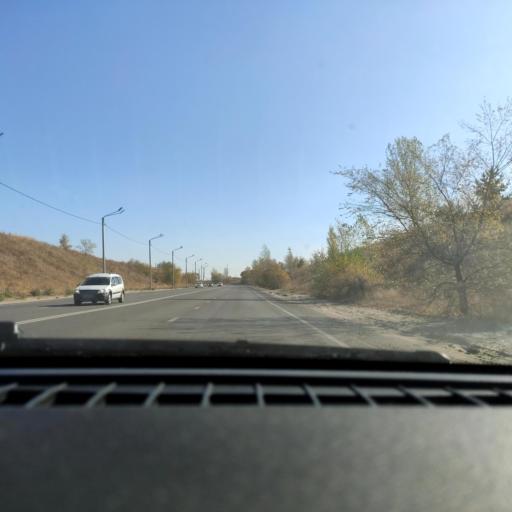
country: RU
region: Voronezj
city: Maslovka
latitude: 51.6216
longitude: 39.2663
